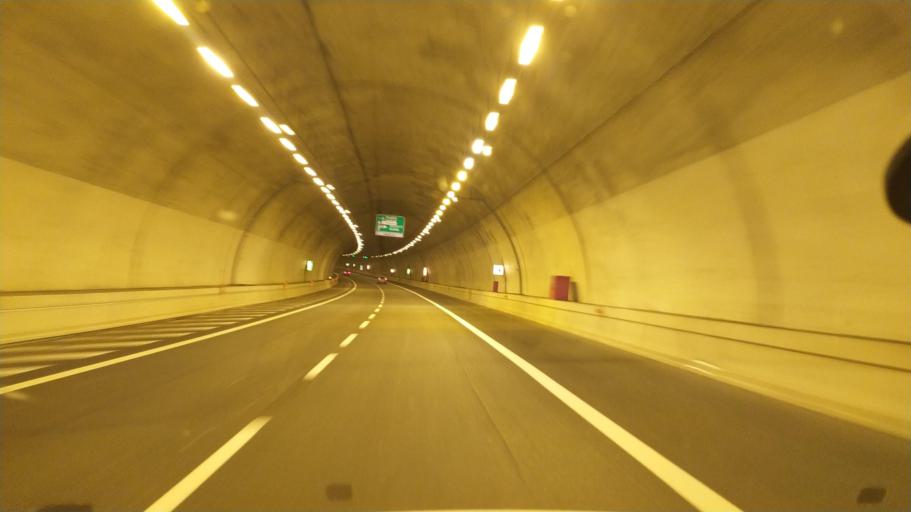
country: IT
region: Lombardy
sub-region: Provincia di Varese
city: Solbiate Olona
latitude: 45.6584
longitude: 8.8862
